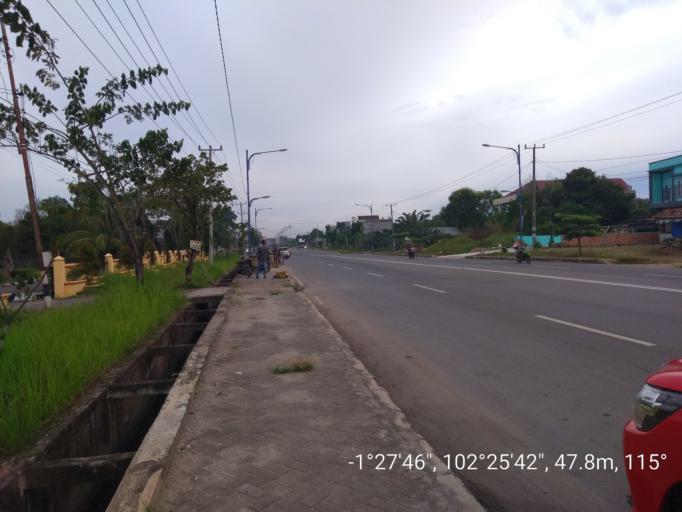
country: ID
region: Jambi
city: Muara Tebo
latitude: -1.4630
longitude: 102.4283
